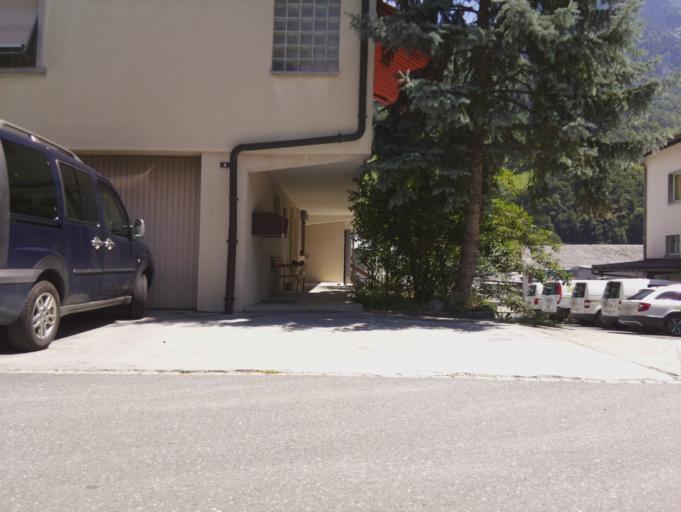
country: CH
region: Glarus
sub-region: Glarus
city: Glarus
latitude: 47.0477
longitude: 9.0632
